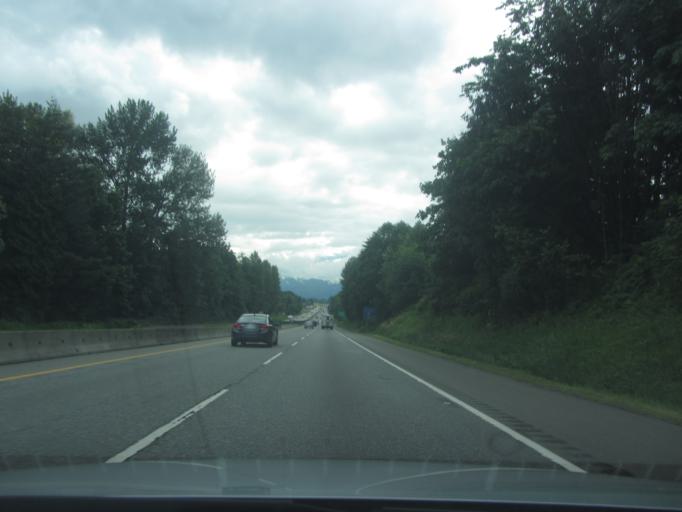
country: CA
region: British Columbia
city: Abbotsford
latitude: 49.0334
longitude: -122.2778
